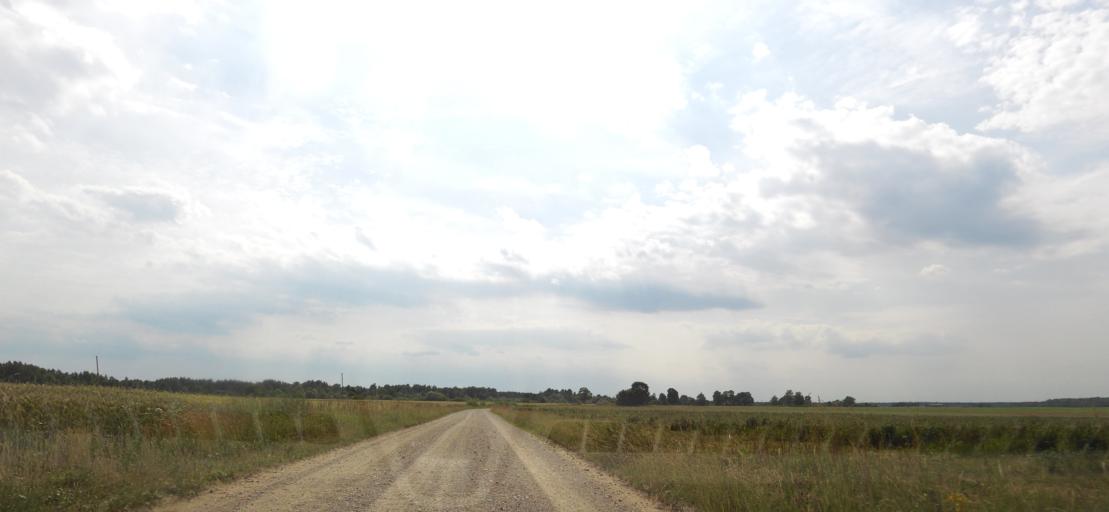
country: LT
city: Obeliai
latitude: 56.1835
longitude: 25.0123
